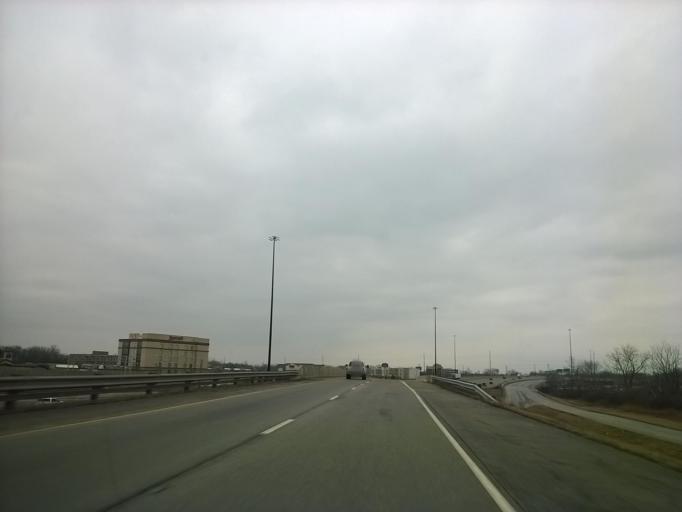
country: US
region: Indiana
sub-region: Marion County
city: Warren Park
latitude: 39.7997
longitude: -86.0381
